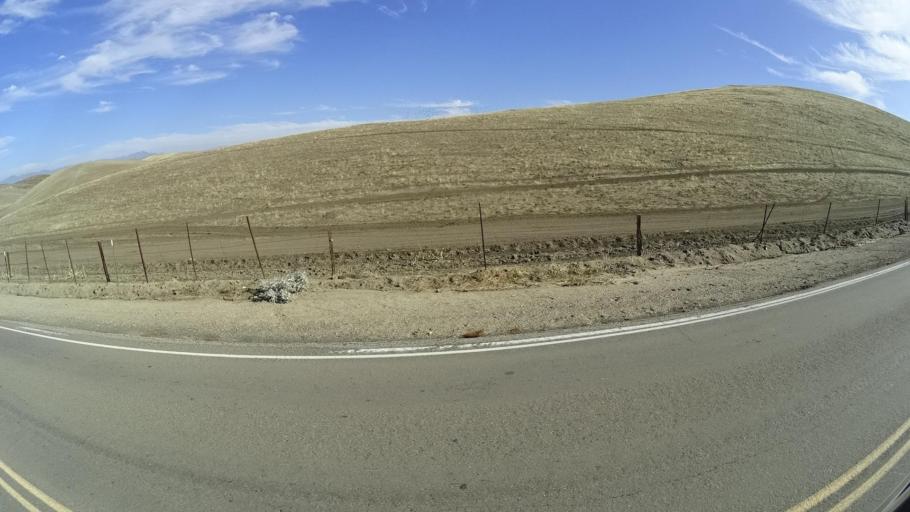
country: US
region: California
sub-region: Kern County
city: Oildale
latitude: 35.5992
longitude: -118.9488
